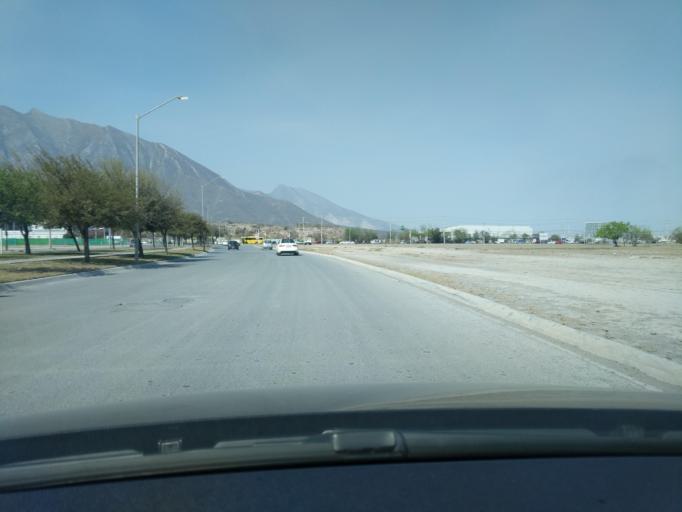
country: MX
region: Nuevo Leon
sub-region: Garcia
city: Los Parques
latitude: 25.7850
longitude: -100.4847
